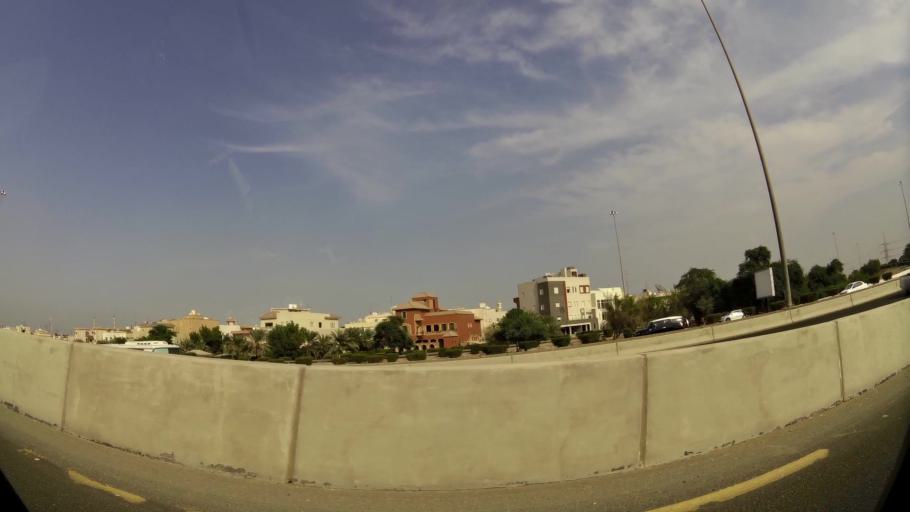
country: KW
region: Al Farwaniyah
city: Al Farwaniyah
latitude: 29.3066
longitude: 47.9780
